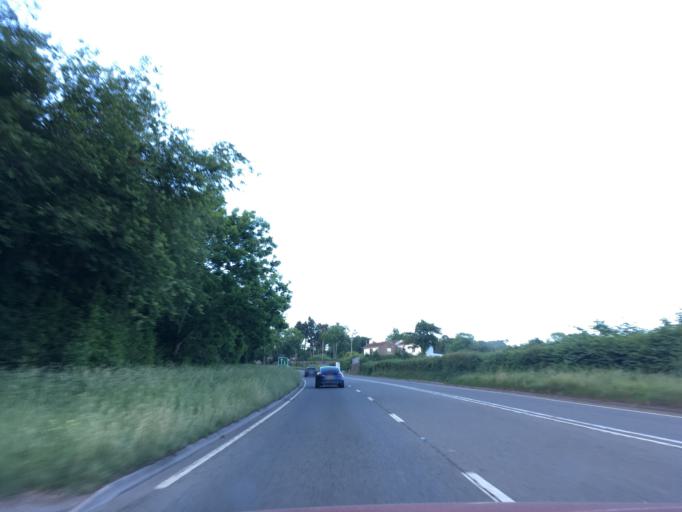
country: GB
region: England
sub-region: North Somerset
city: Butcombe
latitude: 51.3606
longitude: -2.7261
